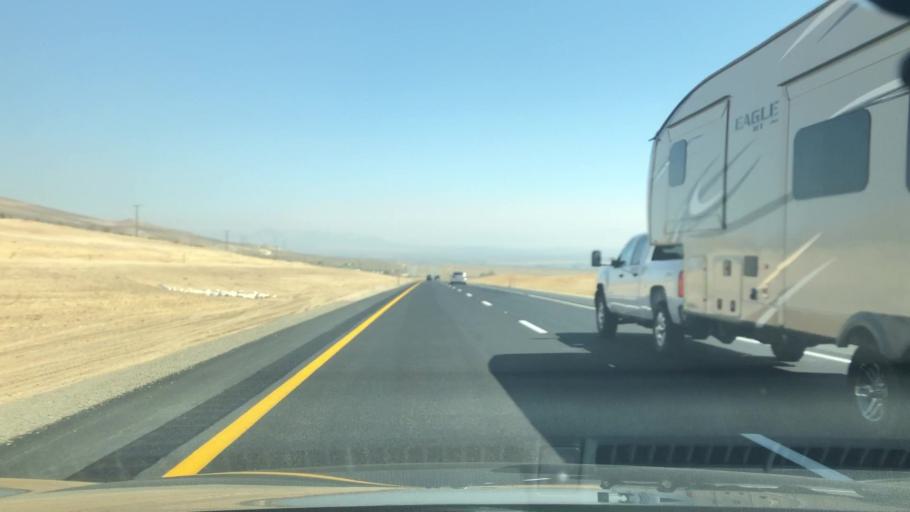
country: US
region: California
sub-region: Kern County
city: Inyokern
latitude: 35.6528
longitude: -117.8776
